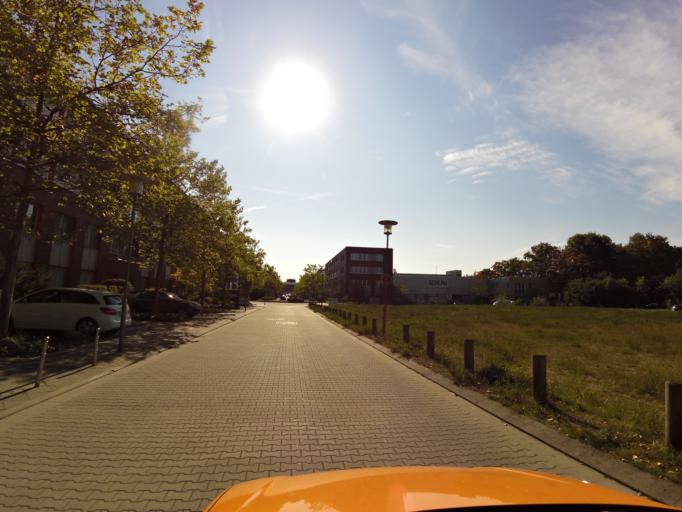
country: DE
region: Berlin
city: Wannsee
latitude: 52.3835
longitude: 13.1178
